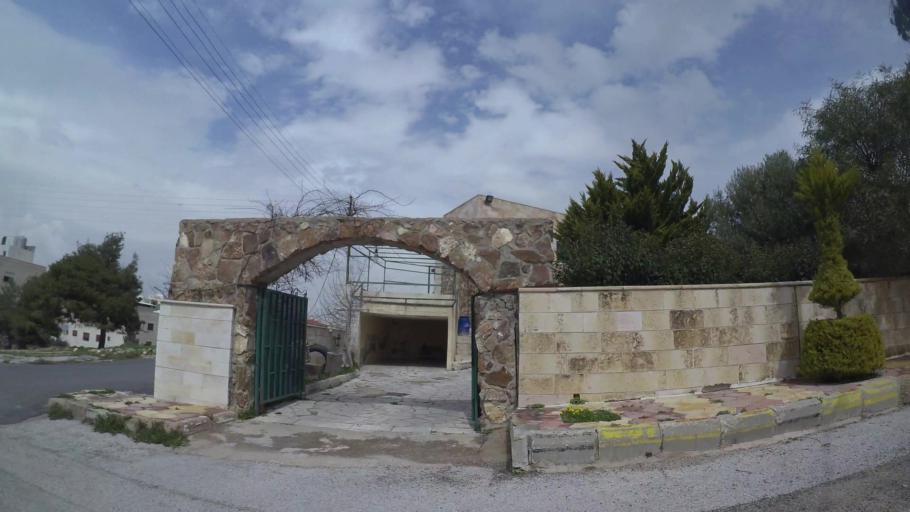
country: JO
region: Amman
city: Umm as Summaq
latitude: 31.8977
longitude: 35.8355
